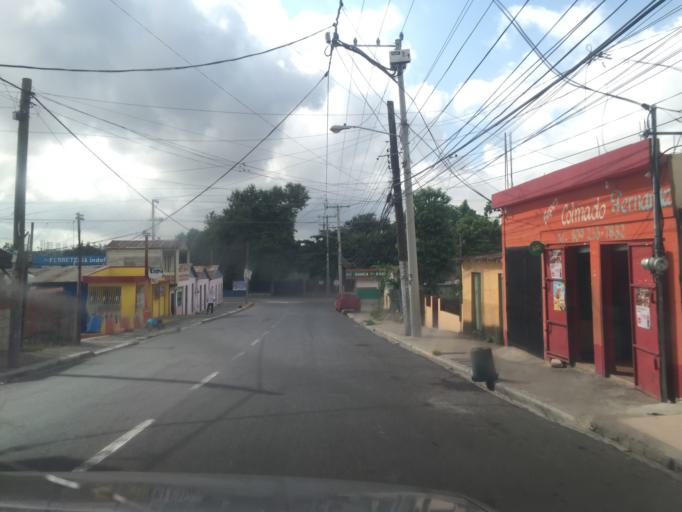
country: DO
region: Santiago
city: Santiago de los Caballeros
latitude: 19.4239
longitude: -70.7140
